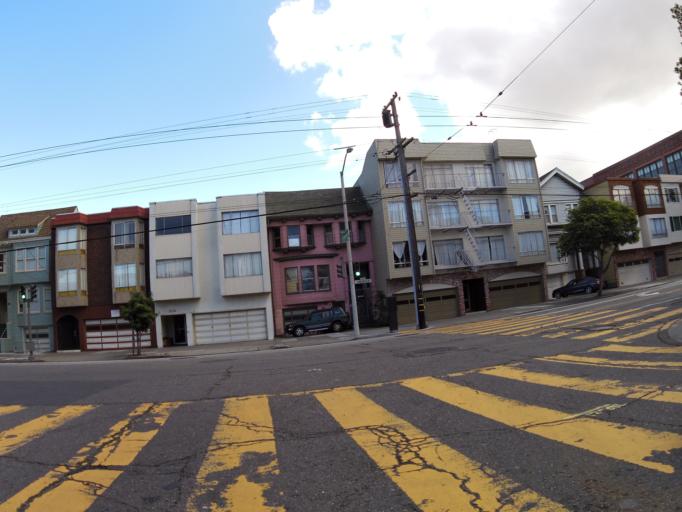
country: US
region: California
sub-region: San Francisco County
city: San Francisco
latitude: 37.7832
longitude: -122.4594
